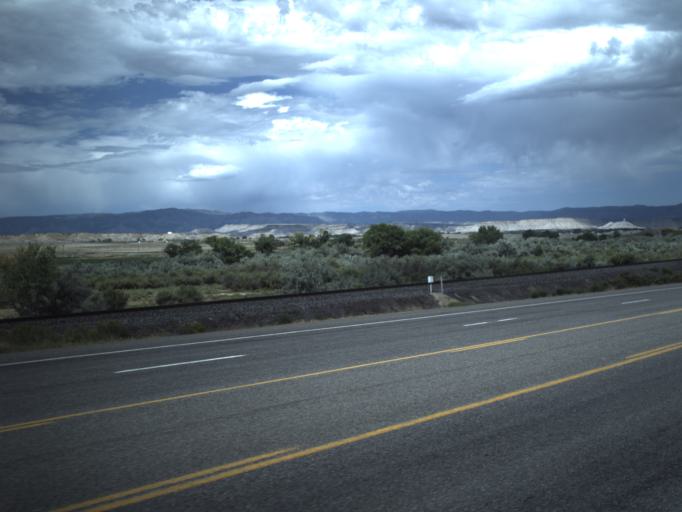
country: US
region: Utah
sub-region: Carbon County
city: Wellington
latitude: 39.5488
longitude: -110.7505
